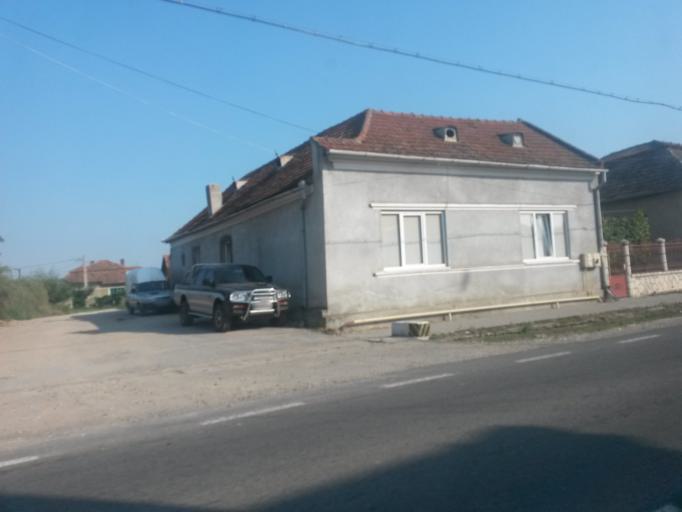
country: RO
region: Alba
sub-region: Comuna Unirea
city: Unirea
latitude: 46.4014
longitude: 23.8100
